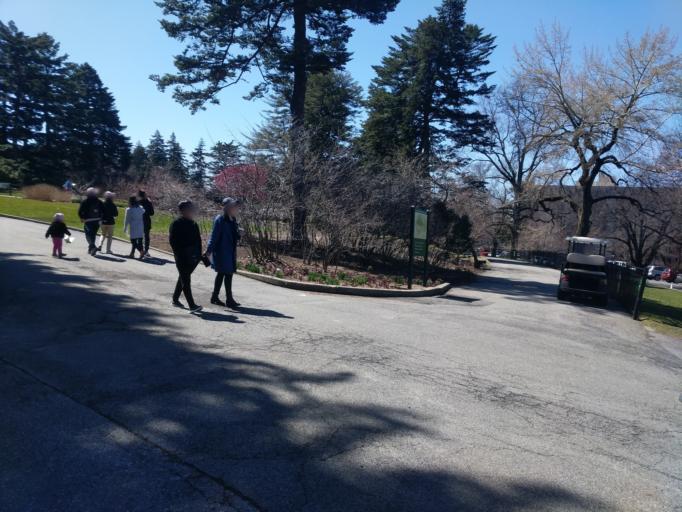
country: US
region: New York
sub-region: Bronx
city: The Bronx
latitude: 40.8656
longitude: -73.8821
